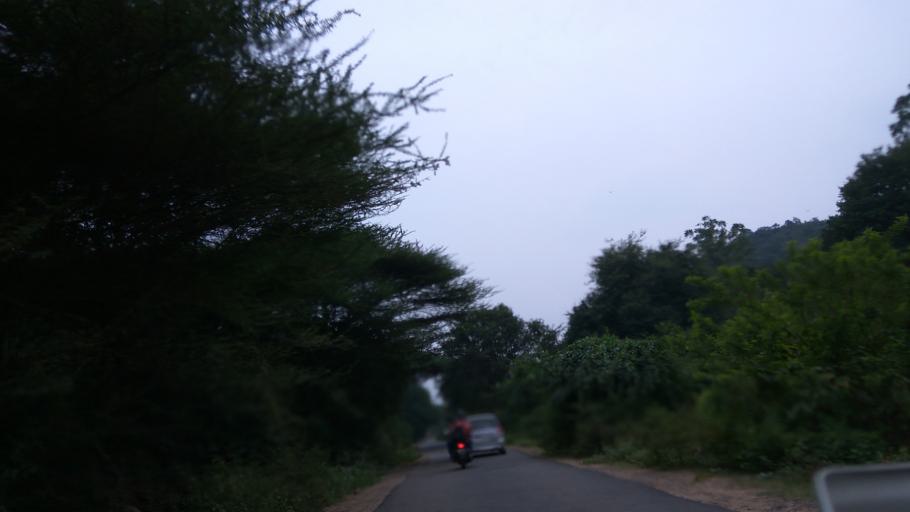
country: IN
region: Tamil Nadu
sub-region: Dharmapuri
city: Mallapuram
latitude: 12.0093
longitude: 78.1343
